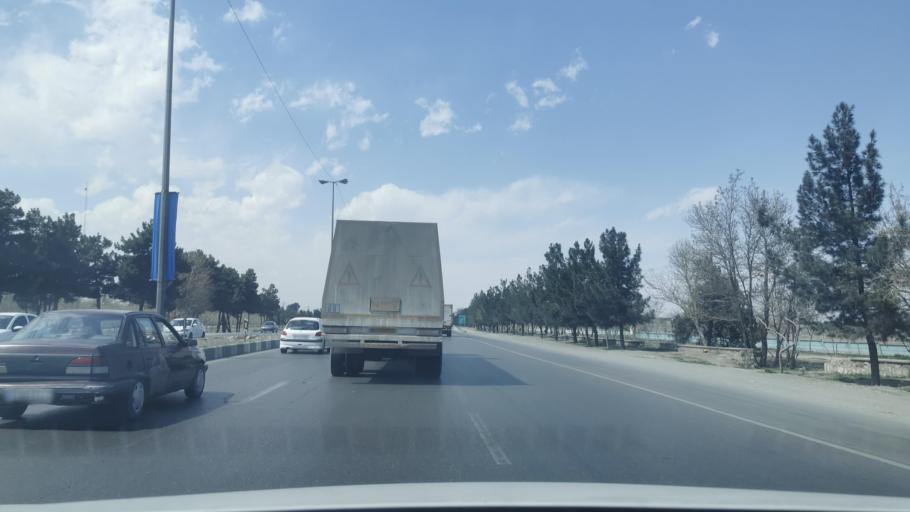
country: IR
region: Razavi Khorasan
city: Torqabeh
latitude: 36.4161
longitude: 59.4673
